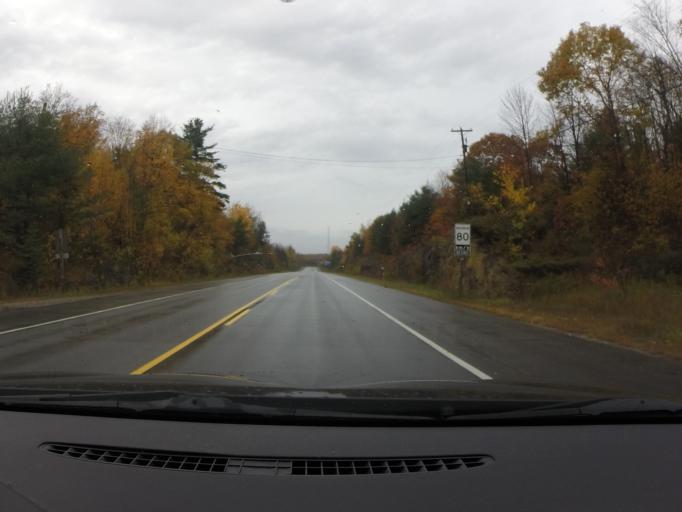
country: CA
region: Ontario
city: Perth
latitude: 44.7971
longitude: -76.6839
